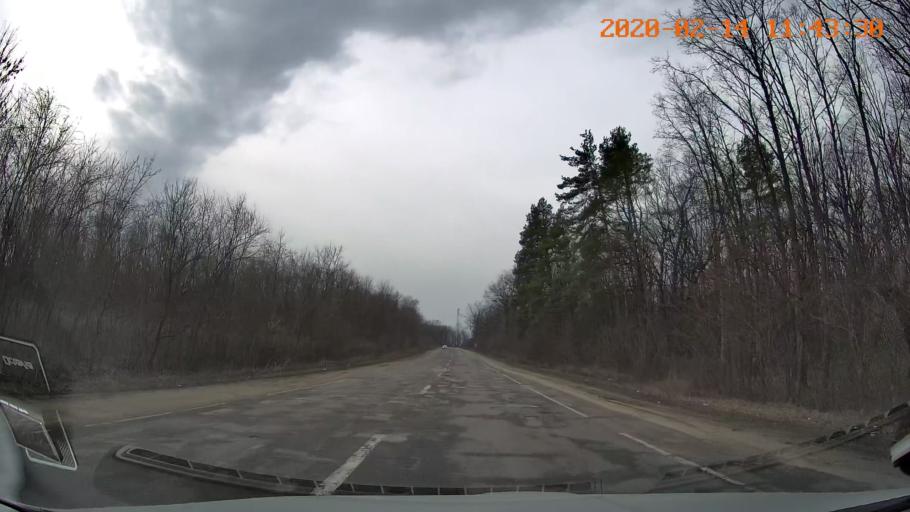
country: MD
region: Briceni
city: Briceni
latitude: 48.3339
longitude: 27.0510
